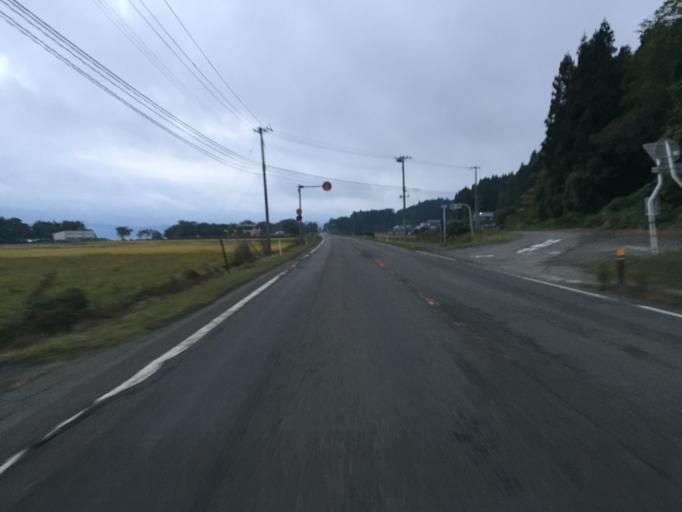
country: JP
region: Fukushima
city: Inawashiro
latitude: 37.5337
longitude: 140.0594
